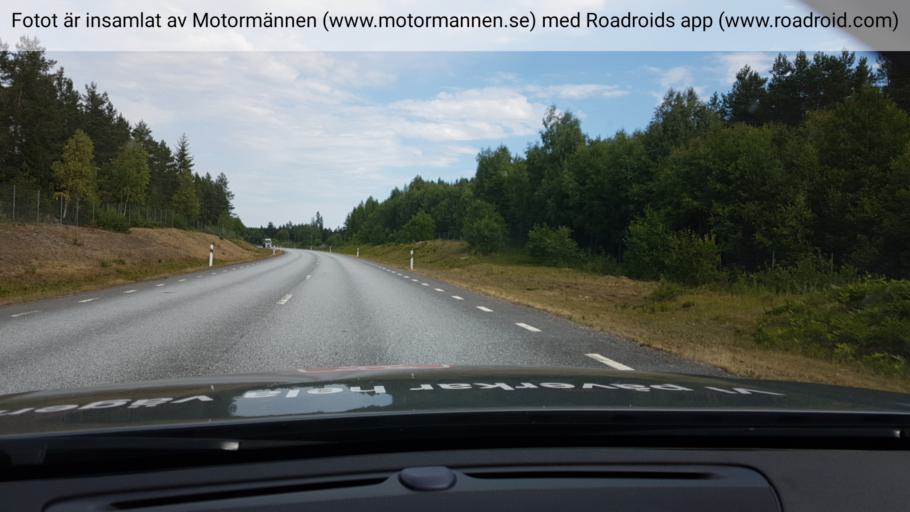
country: SE
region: Uppsala
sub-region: Osthammars Kommun
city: Gimo
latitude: 60.1675
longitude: 18.2782
